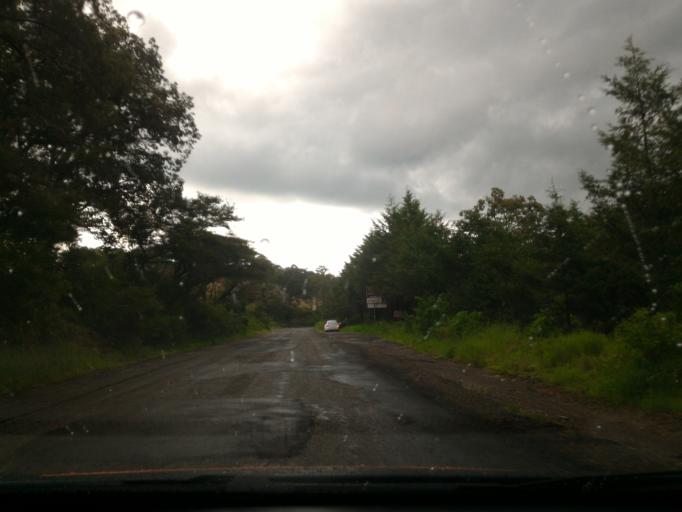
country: MX
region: Jalisco
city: San Andres Ixtlan
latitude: 19.8555
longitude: -103.4559
